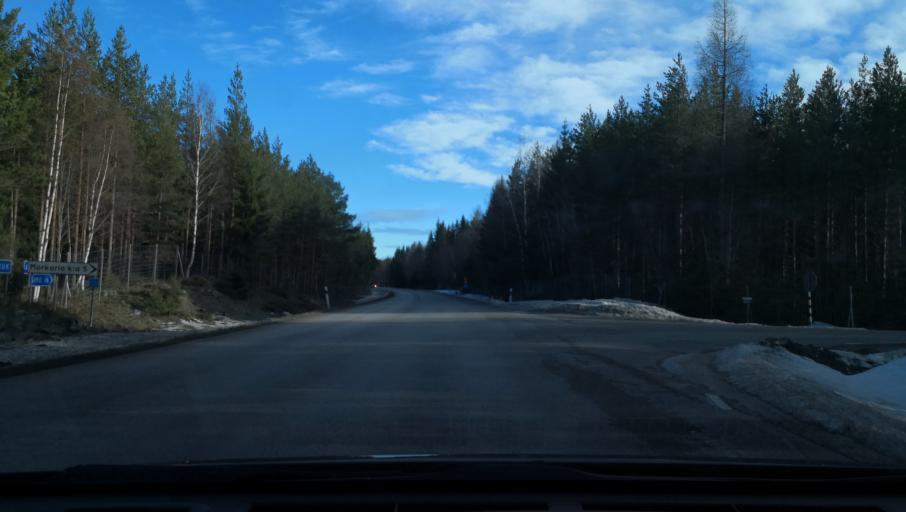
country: SE
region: Uppsala
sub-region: Osthammars Kommun
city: Osterbybruk
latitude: 60.1734
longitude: 17.9246
